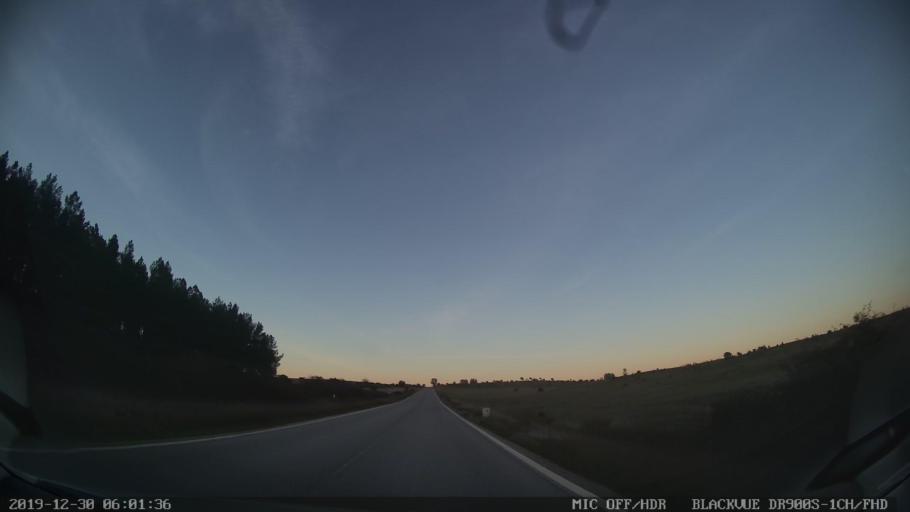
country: PT
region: Castelo Branco
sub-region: Penamacor
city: Penamacor
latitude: 40.0621
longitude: -7.2434
